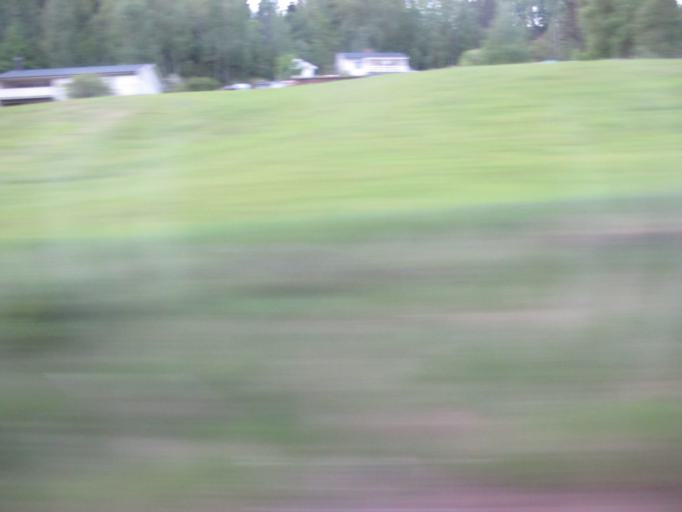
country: NO
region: Oppland
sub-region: Lillehammer
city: Lillehammer
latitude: 61.0900
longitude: 10.4642
